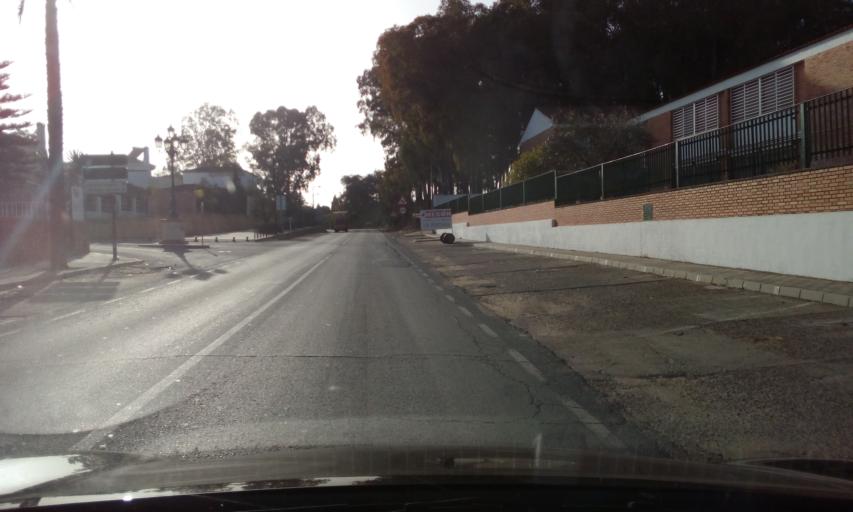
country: ES
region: Andalusia
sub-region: Provincia de Sevilla
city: Olivares
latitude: 37.4142
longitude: -6.1629
